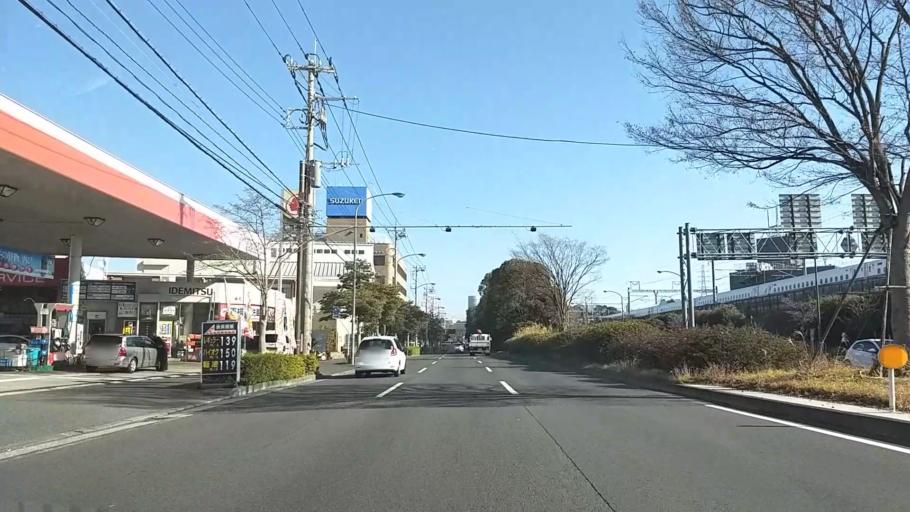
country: JP
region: Kanagawa
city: Yokohama
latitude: 35.4960
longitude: 139.6032
